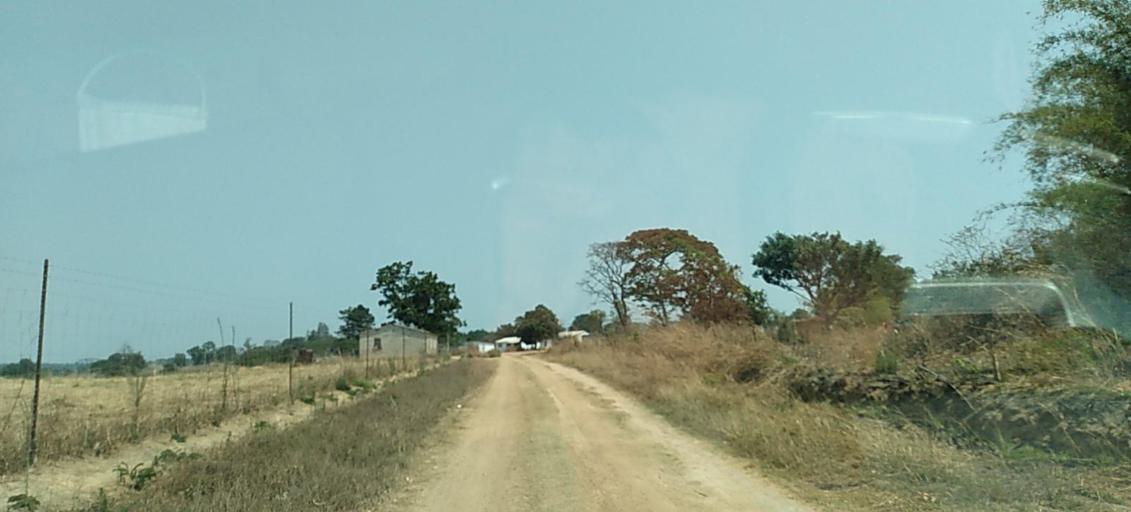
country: ZM
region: Copperbelt
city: Chambishi
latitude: -12.6277
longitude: 27.9407
